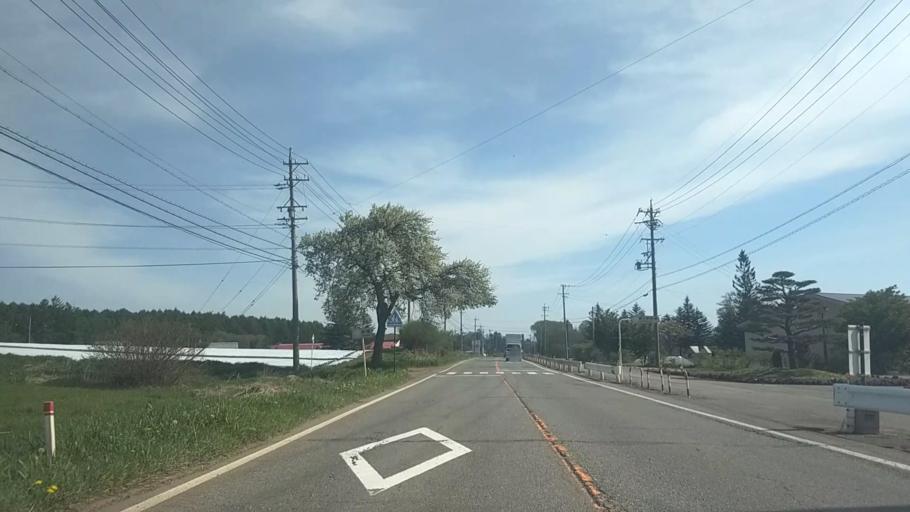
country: JP
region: Nagano
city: Saku
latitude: 35.9679
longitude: 138.4775
